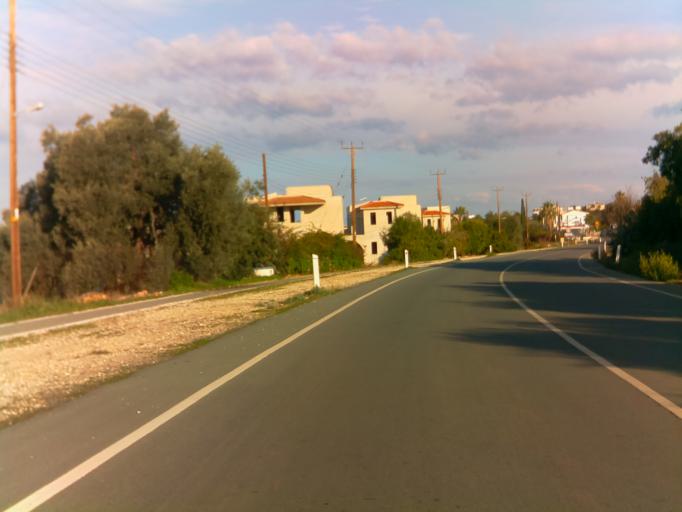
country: CY
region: Pafos
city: Pegeia
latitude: 34.8948
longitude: 32.3336
